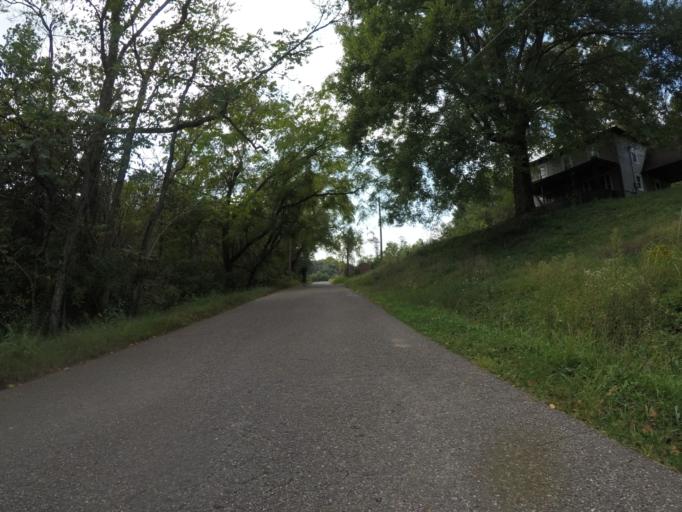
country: US
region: West Virginia
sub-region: Cabell County
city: Huntington
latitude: 38.4529
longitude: -82.4230
